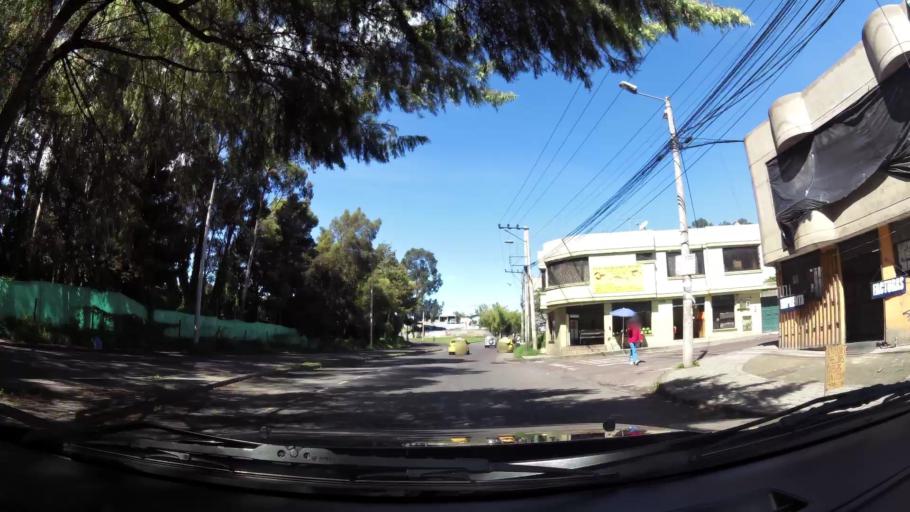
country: EC
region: Pichincha
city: Quito
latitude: -0.2885
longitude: -78.5416
